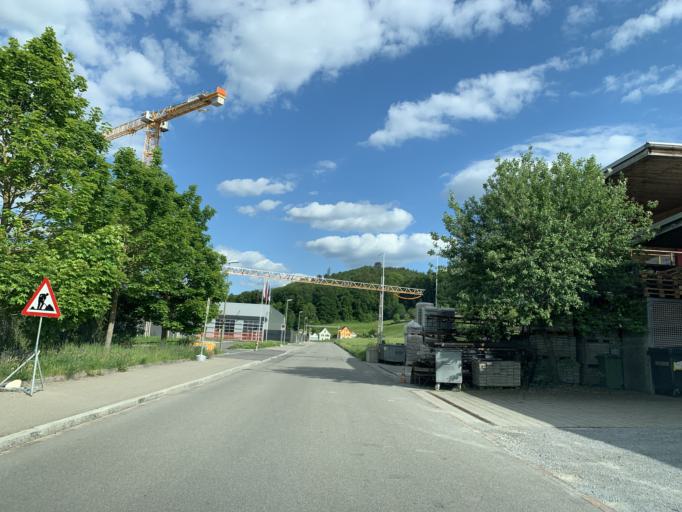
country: CH
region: Zurich
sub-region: Bezirk Winterthur
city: Wuelflingen (Kreis 6) / Niederfeld
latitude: 47.5062
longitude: 8.6779
